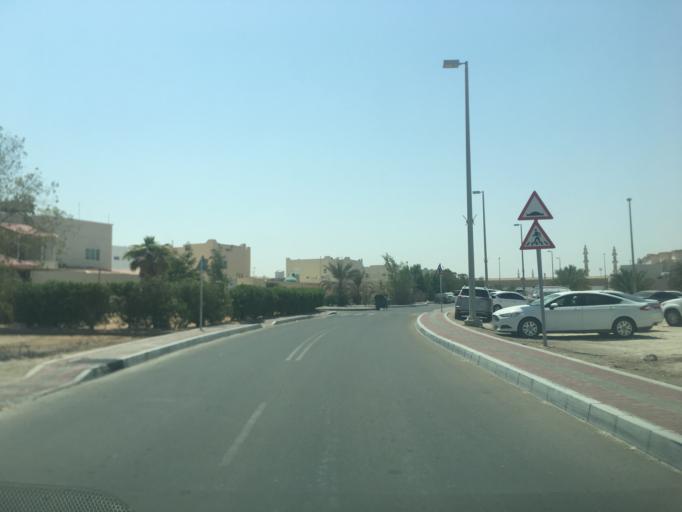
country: AE
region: Abu Dhabi
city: Abu Dhabi
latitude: 24.3068
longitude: 54.6364
